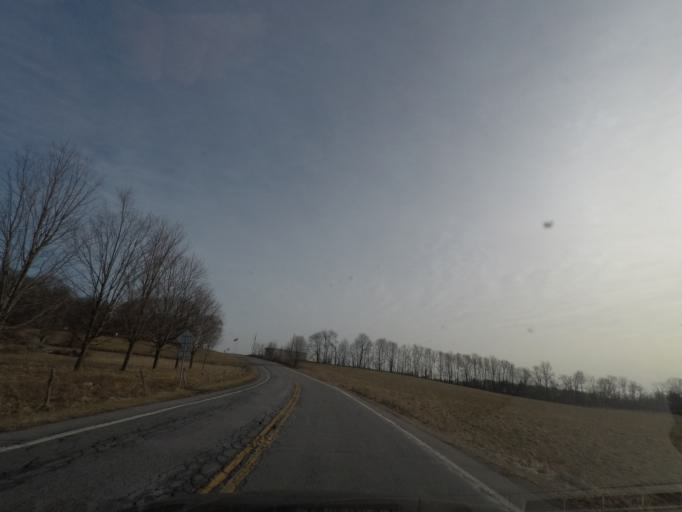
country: US
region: New York
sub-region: Saratoga County
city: Stillwater
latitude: 42.9881
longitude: -73.6970
